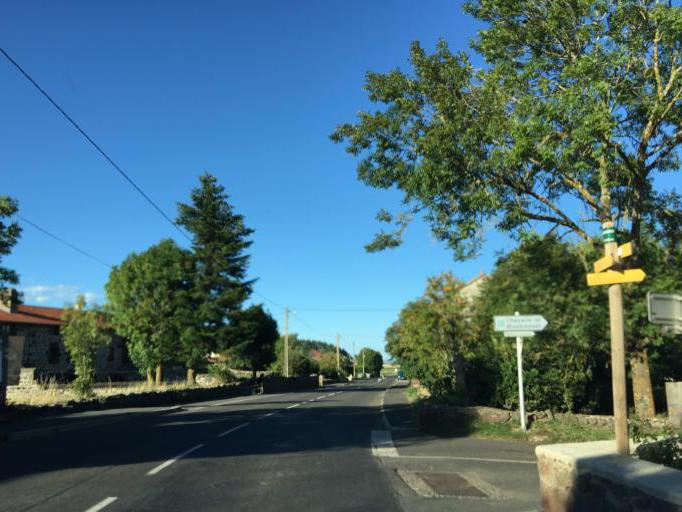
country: FR
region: Auvergne
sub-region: Departement de la Haute-Loire
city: Bains
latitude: 44.9909
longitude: 3.7426
